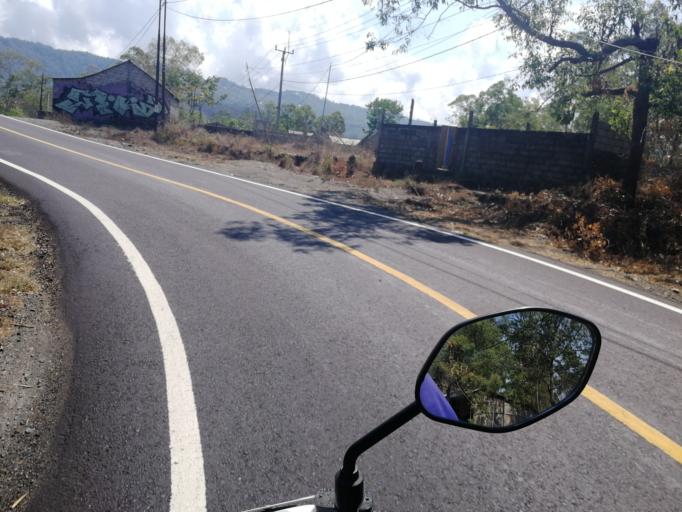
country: ID
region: Bali
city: Banjar Kedisan
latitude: -8.2647
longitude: 115.3866
